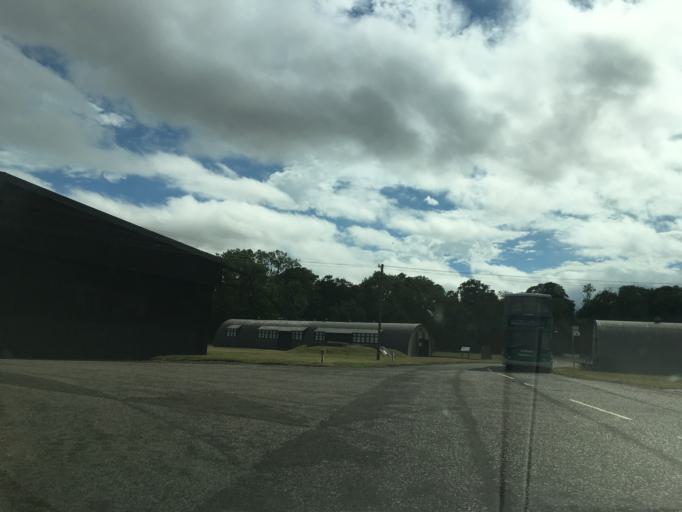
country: GB
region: Scotland
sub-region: East Lothian
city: East Linton
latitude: 55.9955
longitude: -2.7191
